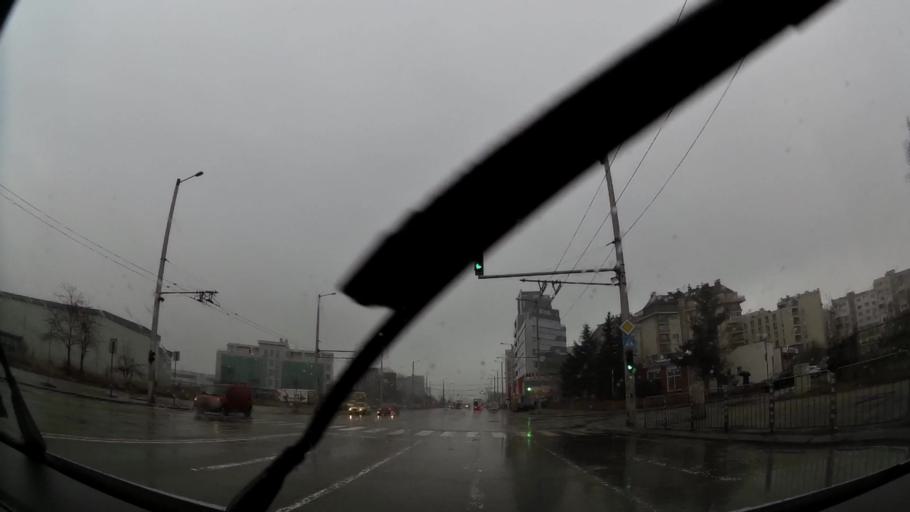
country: BG
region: Sofia-Capital
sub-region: Stolichna Obshtina
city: Sofia
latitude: 42.6525
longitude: 23.4040
